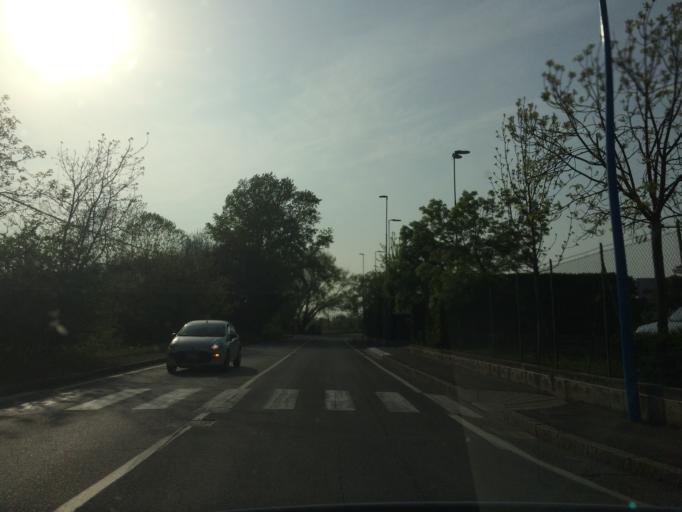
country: IT
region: Lombardy
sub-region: Provincia di Brescia
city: Folzano
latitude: 45.5132
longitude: 10.2059
